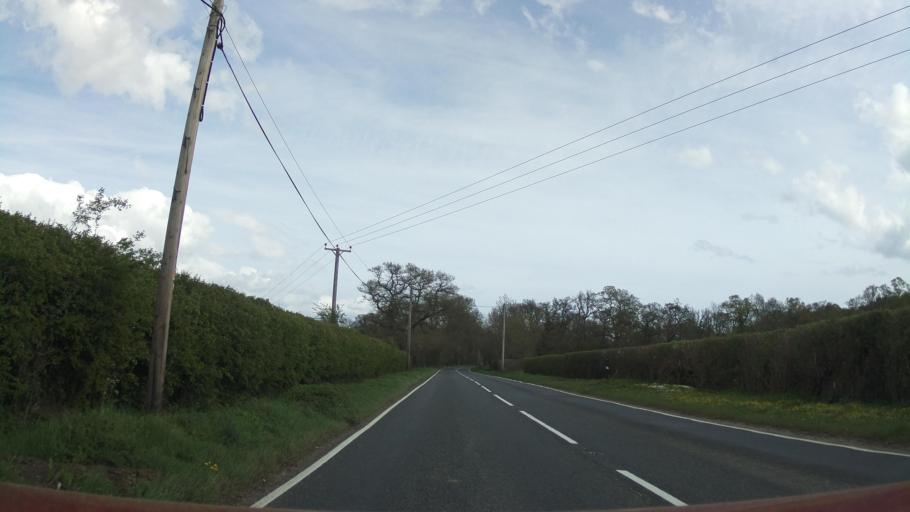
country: GB
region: England
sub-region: Hampshire
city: Chandlers Ford
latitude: 51.0186
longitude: -1.3783
